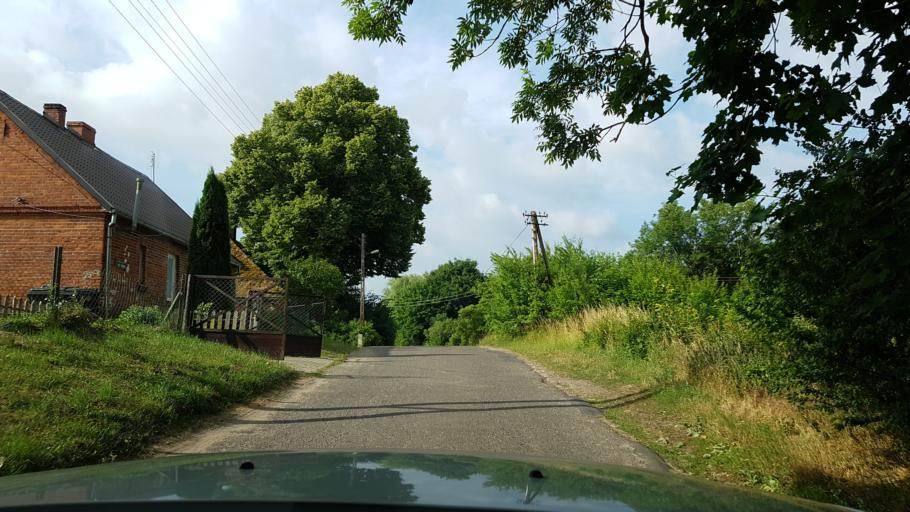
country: PL
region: West Pomeranian Voivodeship
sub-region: Powiat gryfinski
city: Gryfino
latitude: 53.2551
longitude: 14.5536
